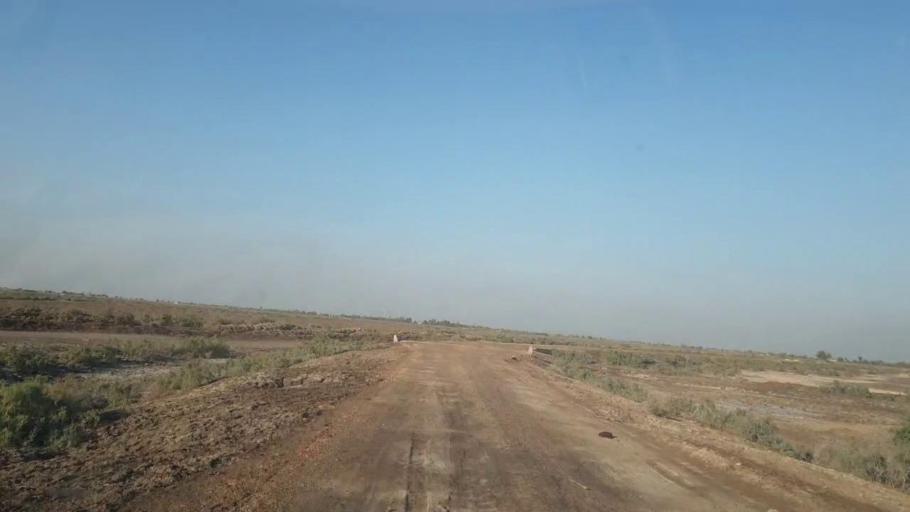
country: PK
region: Sindh
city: Mirpur Khas
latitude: 25.4441
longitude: 69.1024
